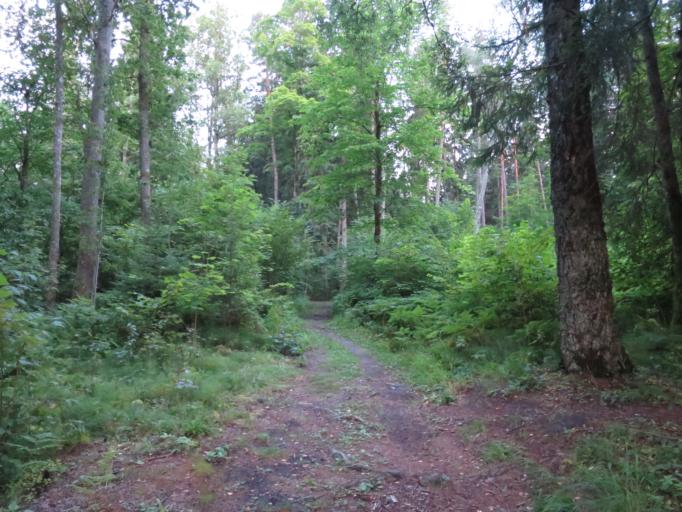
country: LV
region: Sigulda
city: Sigulda
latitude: 57.1427
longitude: 24.8177
